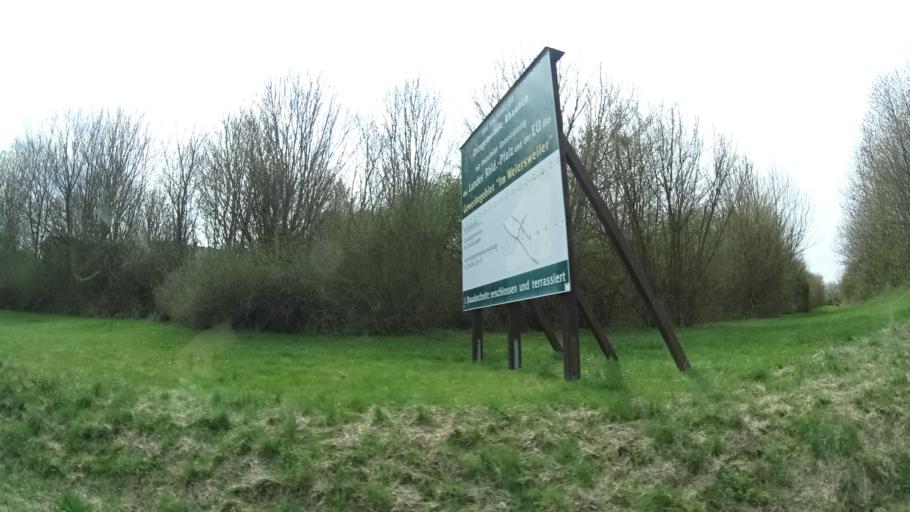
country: DE
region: Rheinland-Pfalz
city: Gosenroth
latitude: 49.8680
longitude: 7.3382
